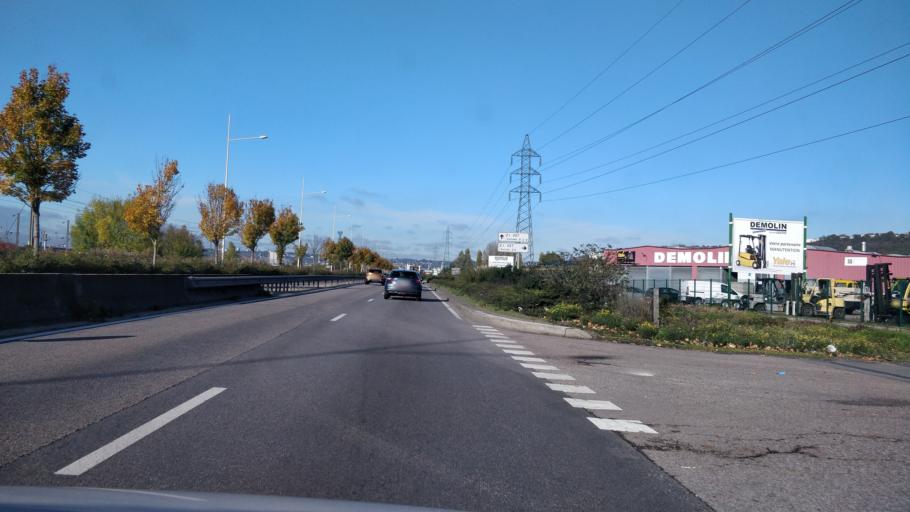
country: FR
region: Haute-Normandie
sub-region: Departement de la Seine-Maritime
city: Sotteville-les-Rouen
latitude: 49.4082
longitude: 1.1095
